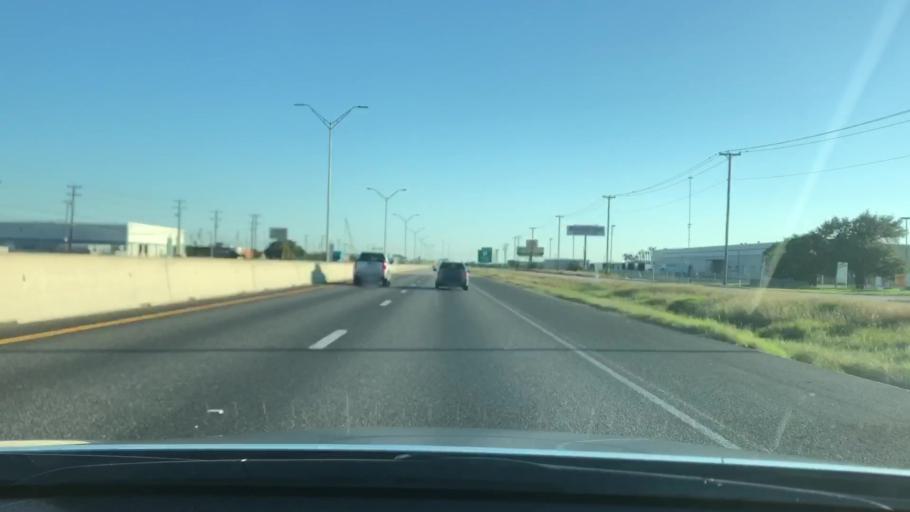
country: US
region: Texas
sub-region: Bexar County
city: Kirby
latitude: 29.4681
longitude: -98.4043
